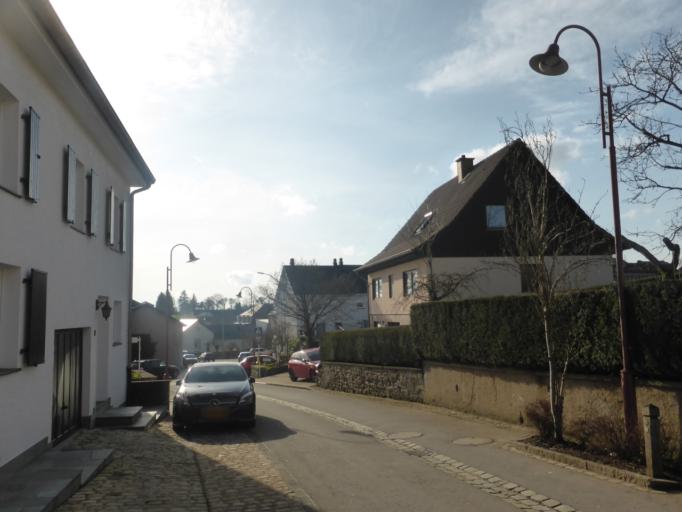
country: LU
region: Diekirch
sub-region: Canton de Redange
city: Grosbous
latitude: 49.8306
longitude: 5.9684
